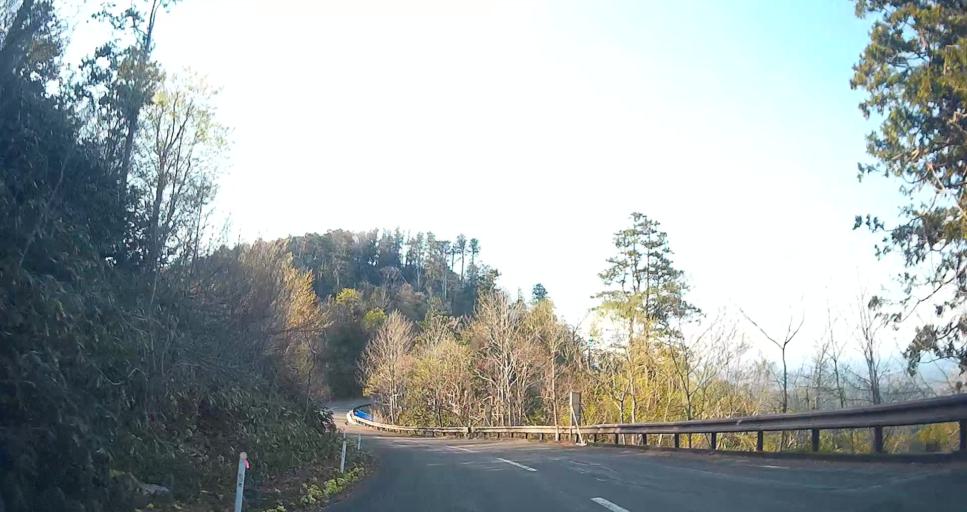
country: JP
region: Aomori
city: Mutsu
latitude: 41.3091
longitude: 141.1134
